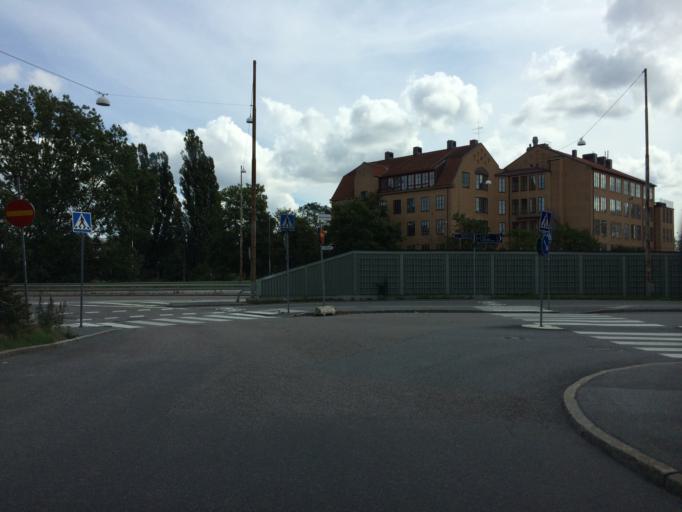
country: SE
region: Stockholm
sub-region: Stockholms Kommun
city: Arsta
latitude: 59.3023
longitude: 18.0172
